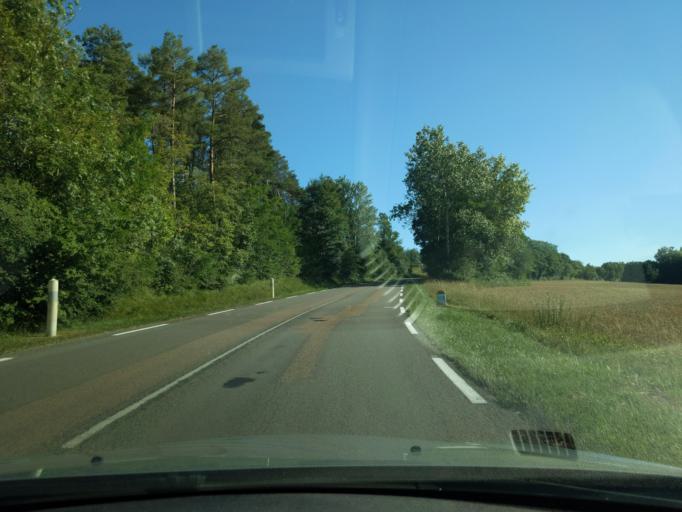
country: FR
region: Bourgogne
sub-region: Departement de la Cote-d'Or
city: Is-sur-Tille
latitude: 47.5074
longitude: 5.0765
